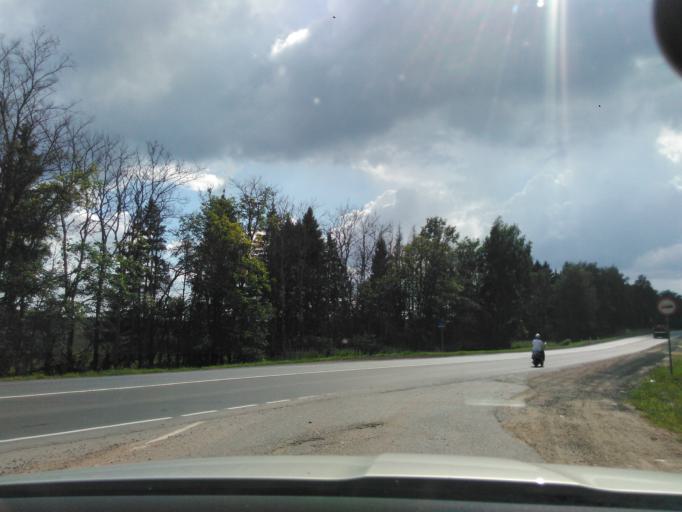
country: RU
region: Moskovskaya
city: Radumlya
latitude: 56.1137
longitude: 37.2133
